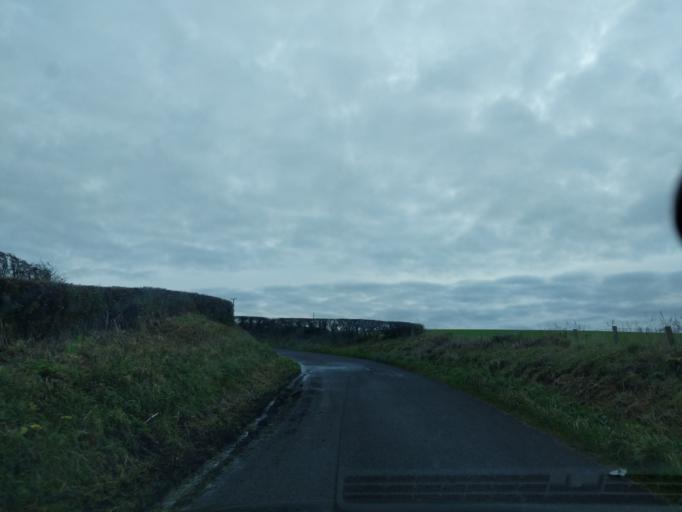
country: GB
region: Scotland
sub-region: West Lothian
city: Linlithgow
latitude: 56.0031
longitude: -3.5753
